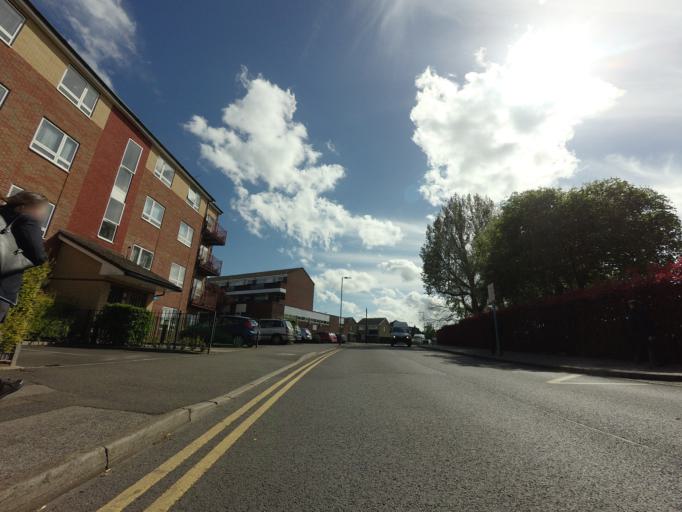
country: GB
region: England
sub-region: Greater London
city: Orpington
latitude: 51.3748
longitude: 0.1162
